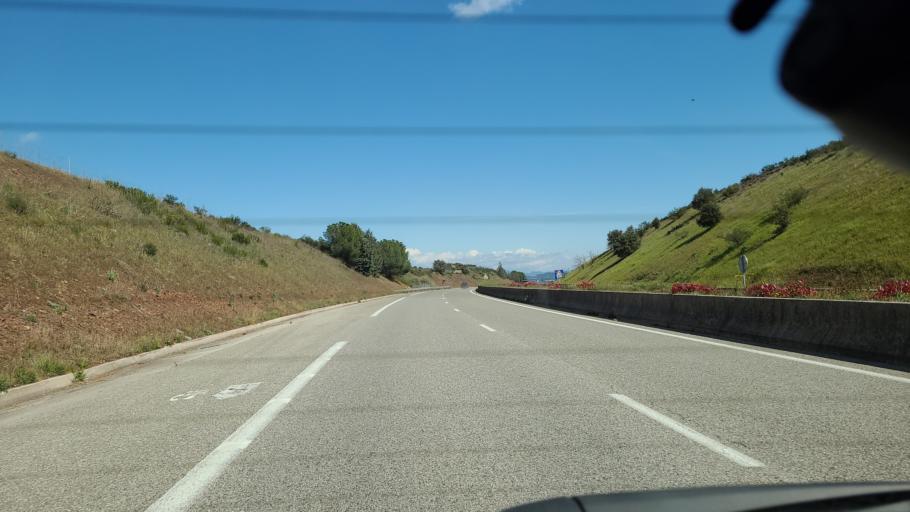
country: FR
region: Provence-Alpes-Cote d'Azur
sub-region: Departement du Var
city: Le Cannet-des-Maures
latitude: 43.3762
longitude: 6.3493
